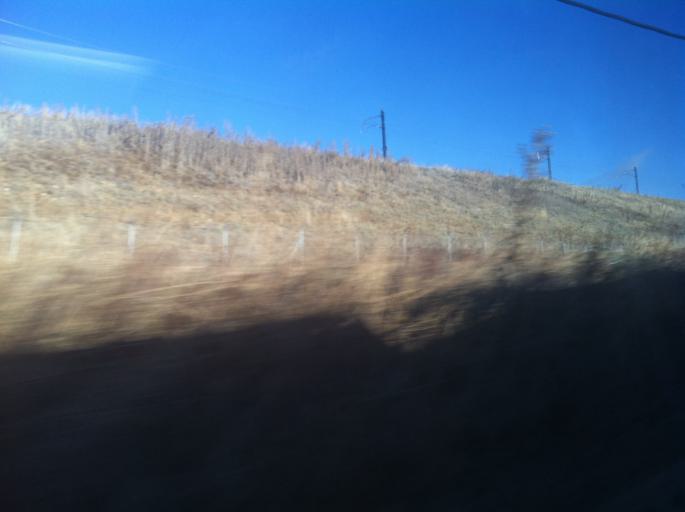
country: ES
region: Castille and Leon
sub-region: Provincia de Palencia
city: Palenzuela
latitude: 42.1176
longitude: -4.1578
